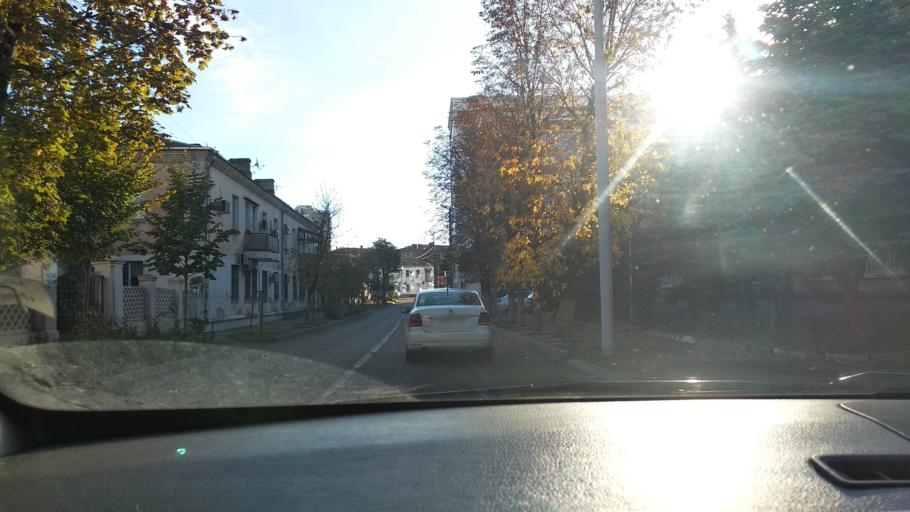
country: RU
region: Krasnodarskiy
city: Krasnodar
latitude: 45.0212
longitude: 38.9796
